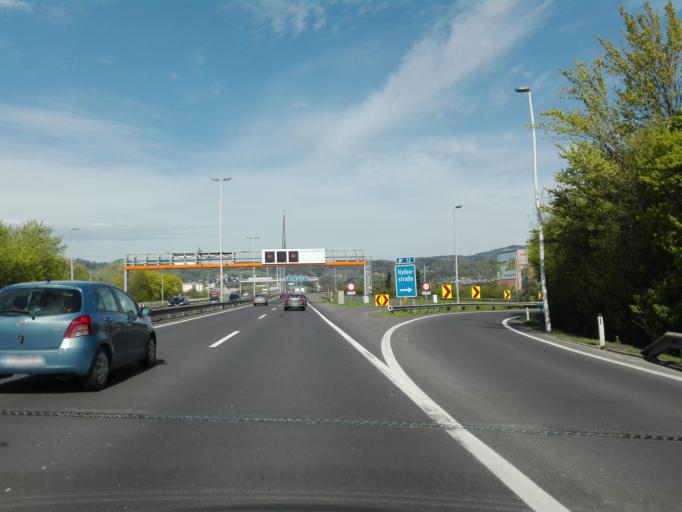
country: AT
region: Upper Austria
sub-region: Linz Stadt
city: Linz
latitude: 48.3174
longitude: 14.3032
